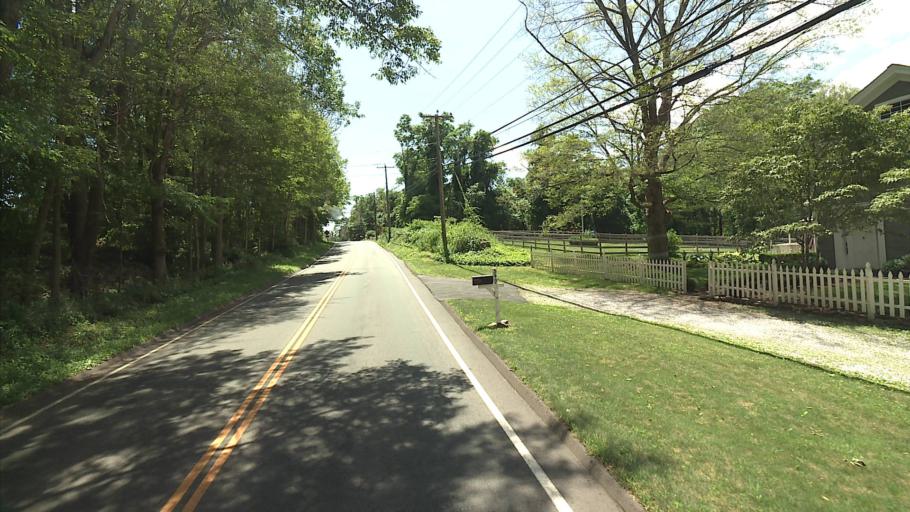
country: US
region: Connecticut
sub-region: Middlesex County
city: Moodus
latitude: 41.4873
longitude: -72.4470
